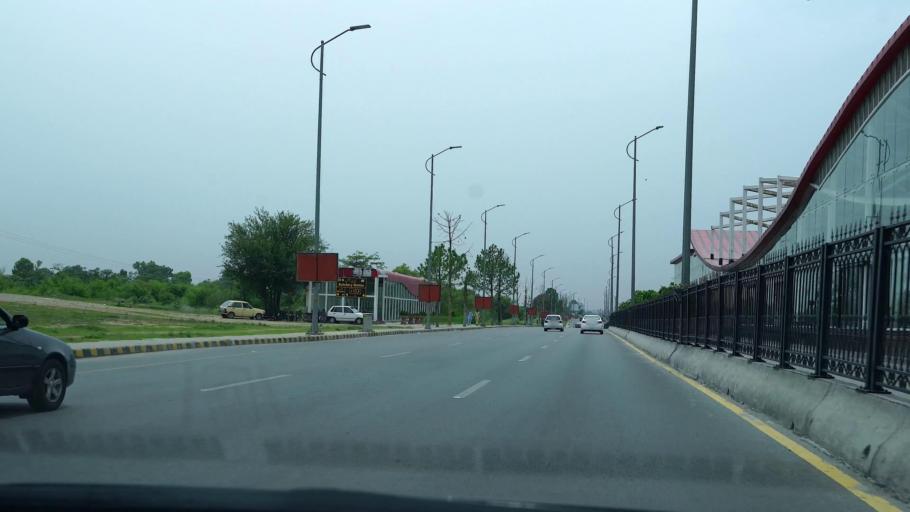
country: PK
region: Islamabad
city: Islamabad
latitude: 33.7058
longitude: 73.0484
